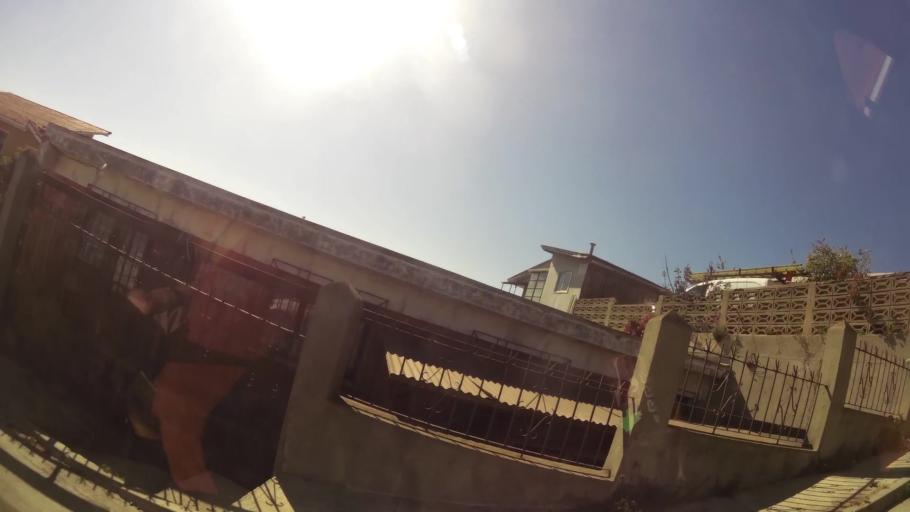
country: CL
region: Valparaiso
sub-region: Provincia de Valparaiso
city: Valparaiso
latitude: -33.0498
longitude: -71.6378
